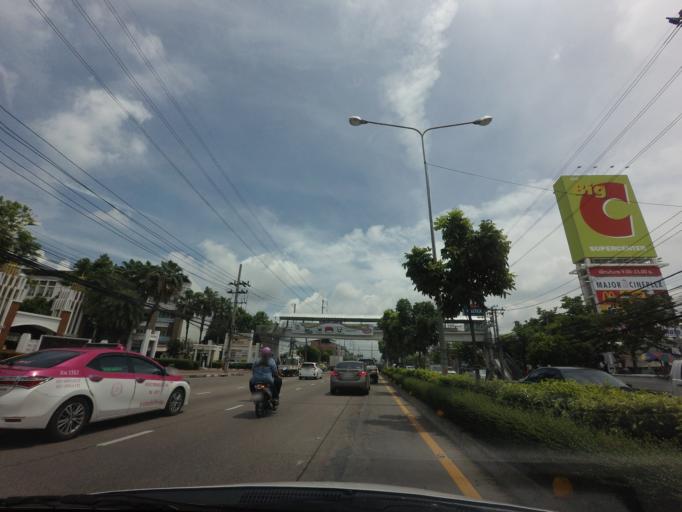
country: TH
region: Samut Prakan
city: Phra Pradaeng
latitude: 13.6534
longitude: 100.5211
